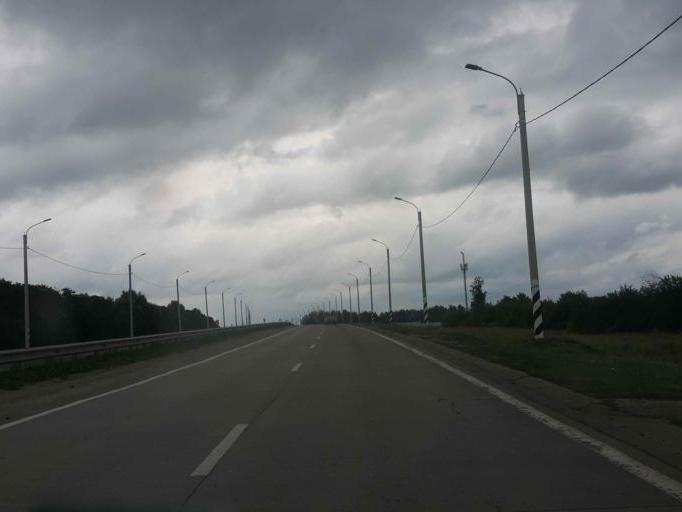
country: RU
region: Tambov
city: Selezni
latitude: 52.7444
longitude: 41.1993
